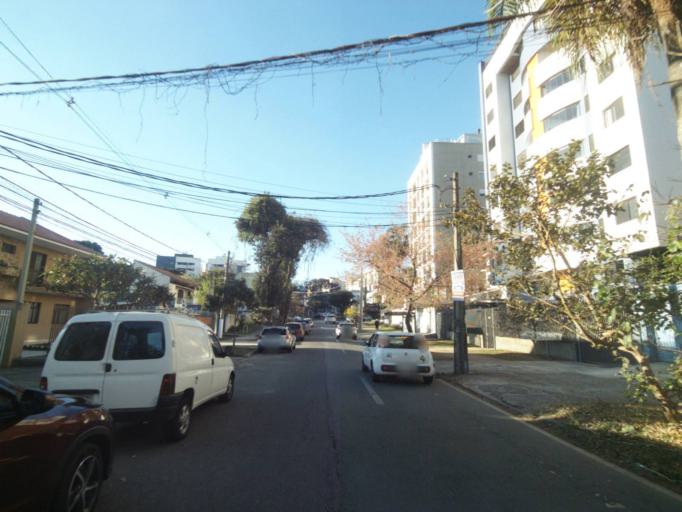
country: BR
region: Parana
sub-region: Curitiba
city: Curitiba
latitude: -25.4555
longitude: -49.2916
